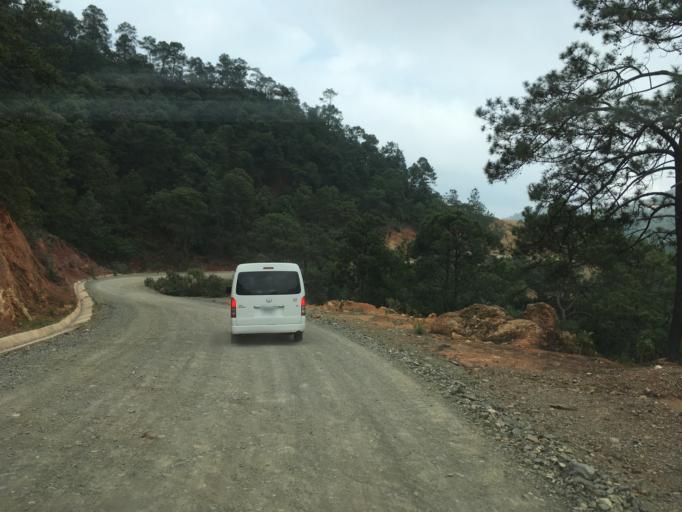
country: MX
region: Oaxaca
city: Santiago Tilantongo
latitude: 17.2011
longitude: -97.2802
